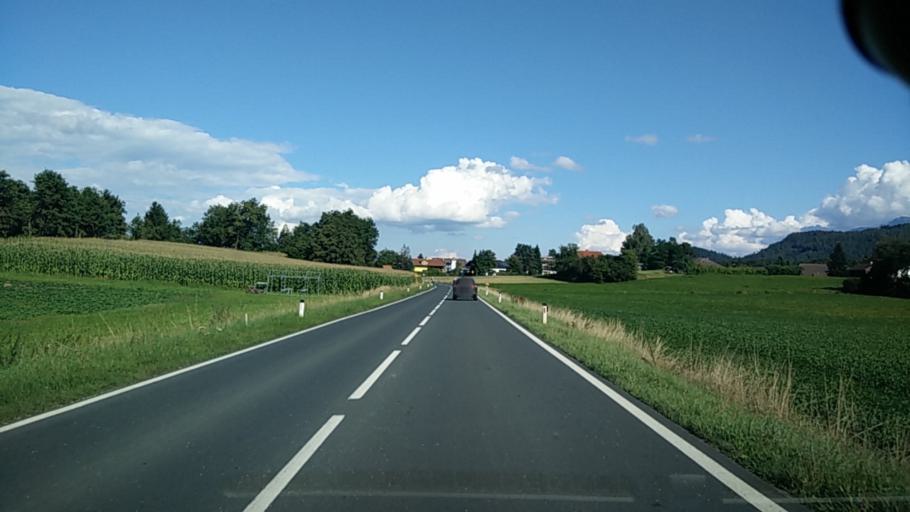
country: AT
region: Carinthia
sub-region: Politischer Bezirk Volkermarkt
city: Eberndorf
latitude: 46.6154
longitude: 14.5662
